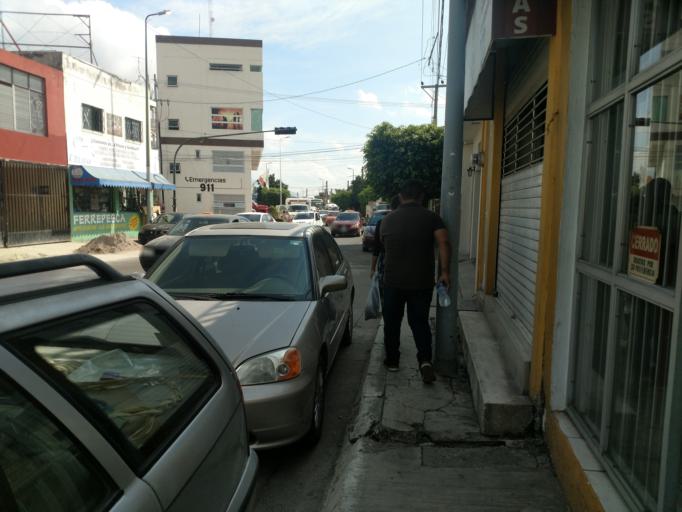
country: MX
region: Nayarit
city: Tepic
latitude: 21.5139
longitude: -104.8887
